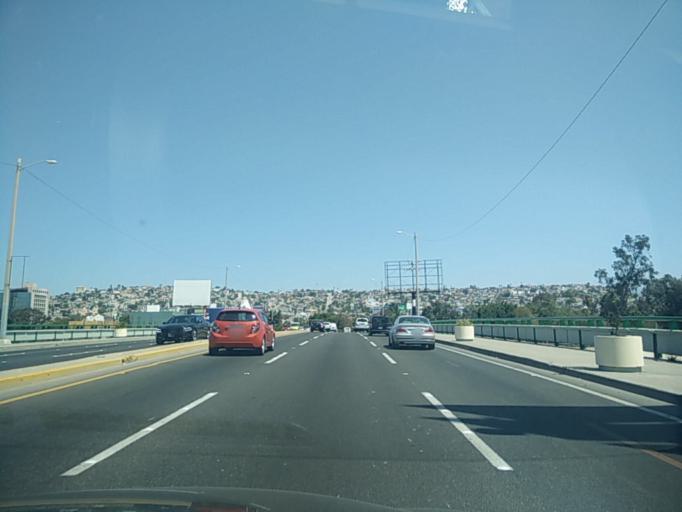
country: MX
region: Baja California
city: Tijuana
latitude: 32.5269
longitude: -117.0156
